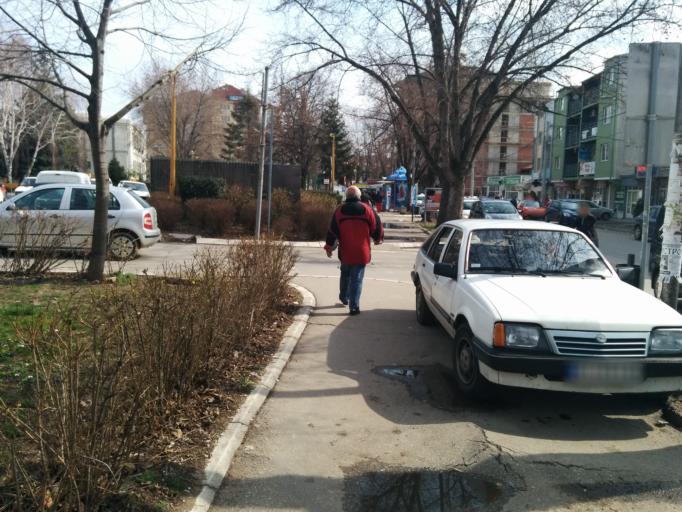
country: RS
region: Central Serbia
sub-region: Nisavski Okrug
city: Nis
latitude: 43.3228
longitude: 21.9069
